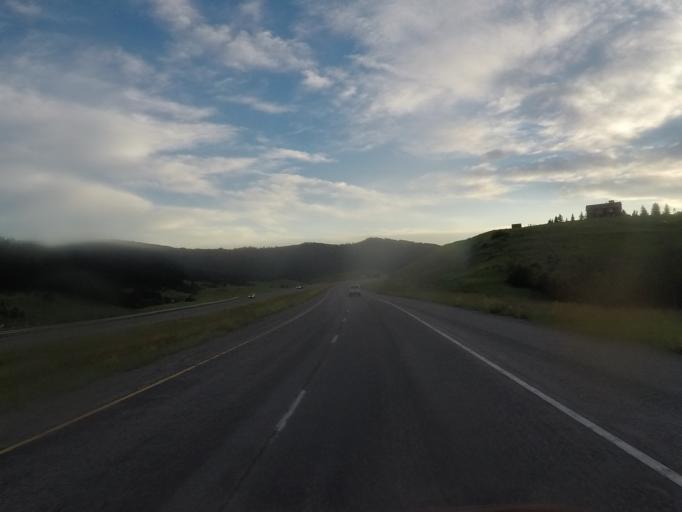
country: US
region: Montana
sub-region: Park County
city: Livingston
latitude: 45.6615
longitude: -110.7463
